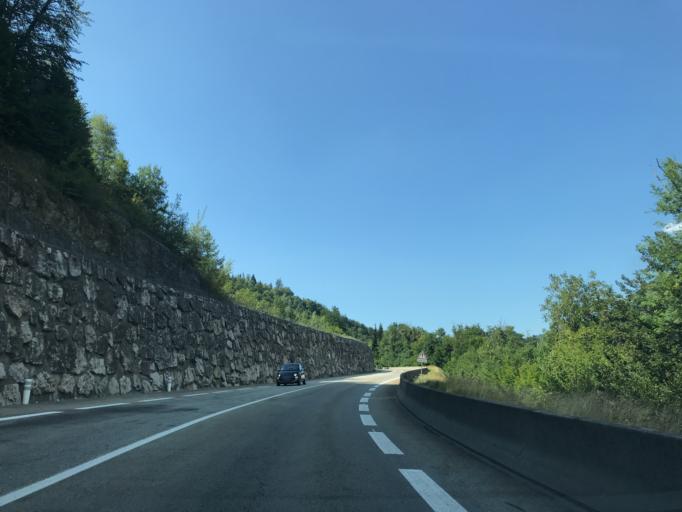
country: FR
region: Rhone-Alpes
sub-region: Departement de la Haute-Savoie
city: Dingy-Saint-Clair
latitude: 45.9086
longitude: 6.1988
